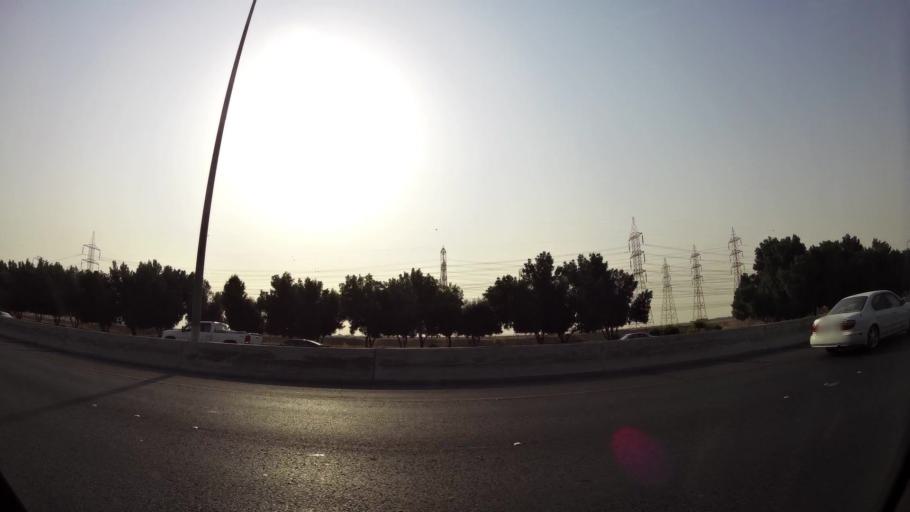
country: KW
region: Mubarak al Kabir
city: Mubarak al Kabir
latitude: 29.2163
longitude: 48.0569
